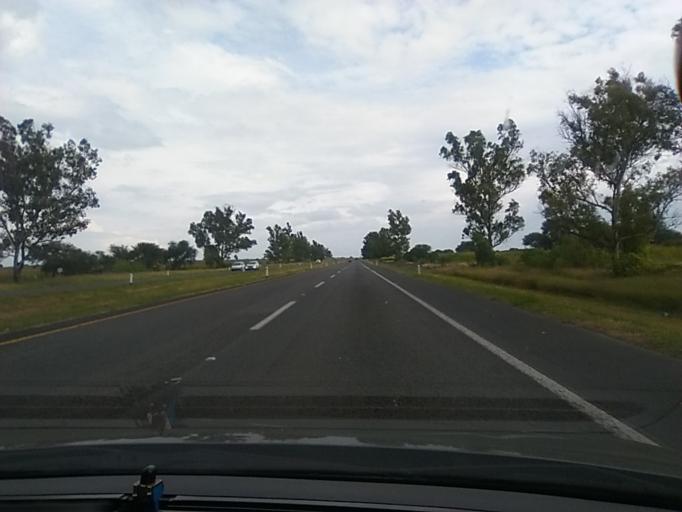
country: MX
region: Jalisco
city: Jamay
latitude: 20.3569
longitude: -102.6406
